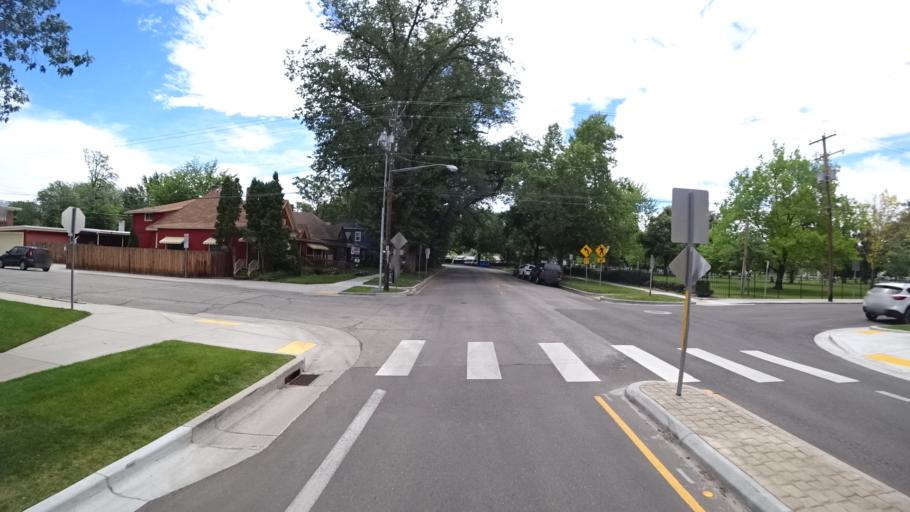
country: US
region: Idaho
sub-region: Ada County
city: Boise
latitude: 43.6121
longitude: -116.1898
